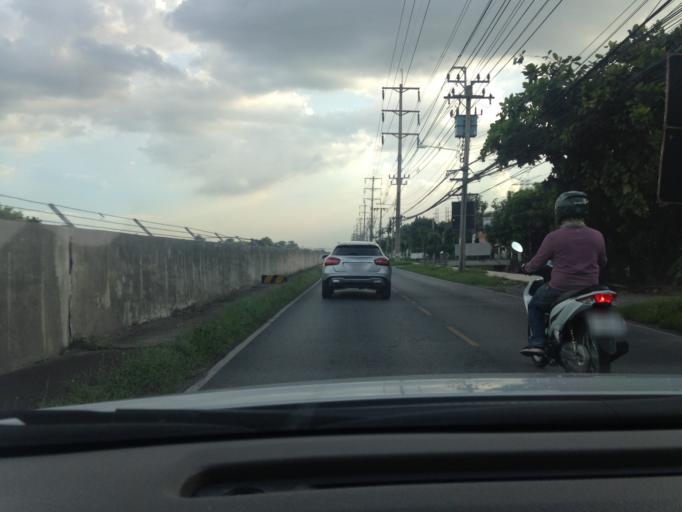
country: TH
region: Bangkok
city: Don Mueang
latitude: 13.9137
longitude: 100.5587
